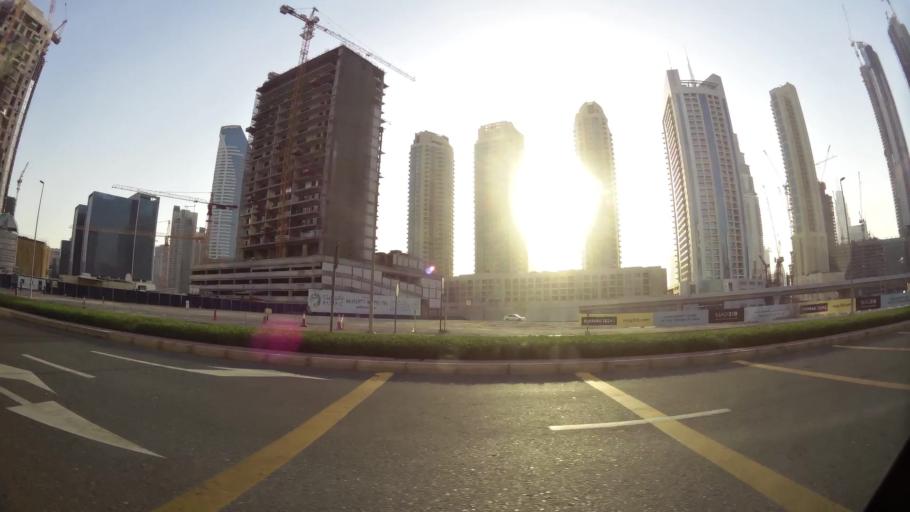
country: AE
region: Dubai
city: Dubai
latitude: 25.1900
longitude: 55.2840
